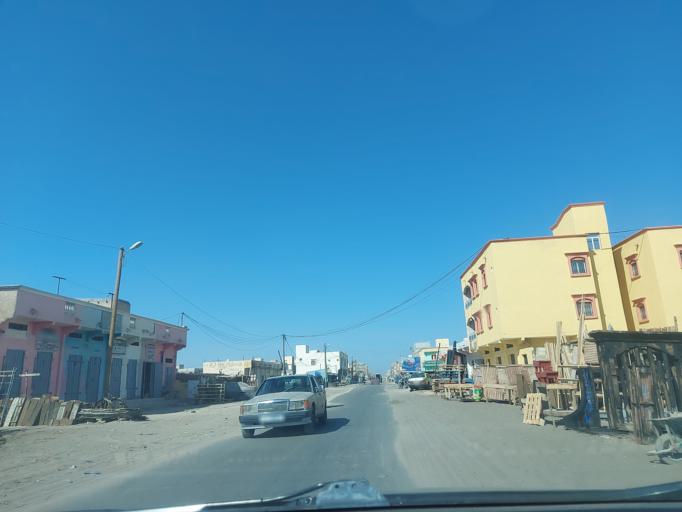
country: MR
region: Nouakchott
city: Nouakchott
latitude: 18.0669
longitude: -15.9967
